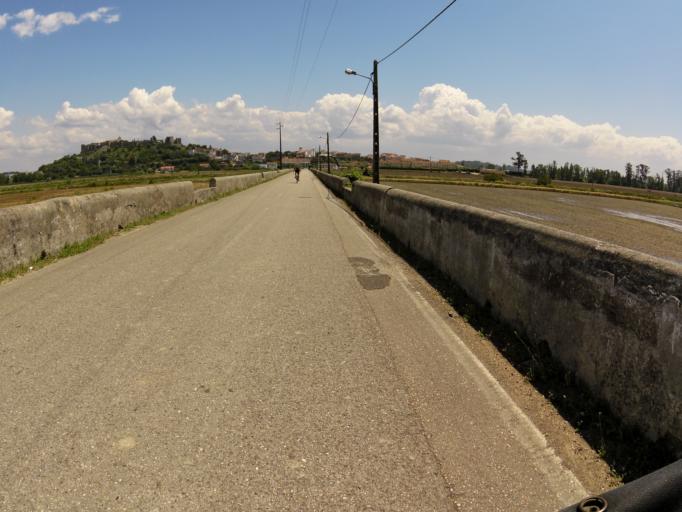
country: PT
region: Coimbra
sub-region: Montemor-O-Velho
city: Montemor-o-Velho
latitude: 40.1764
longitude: -8.6937
